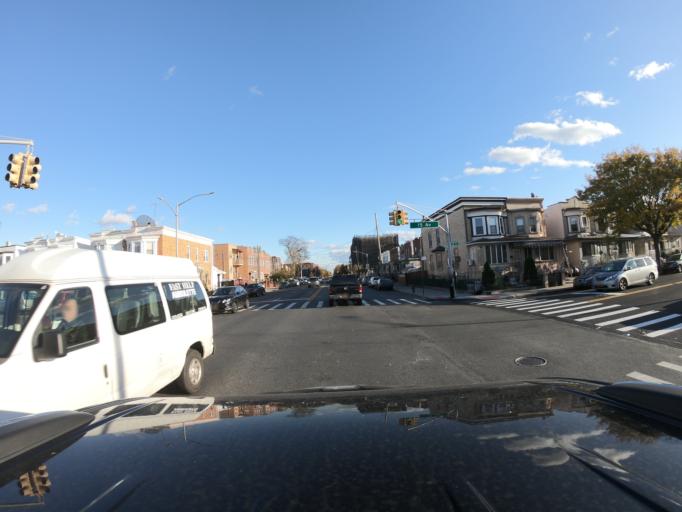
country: US
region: New York
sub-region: Kings County
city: Bensonhurst
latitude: 40.6233
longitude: -73.9971
